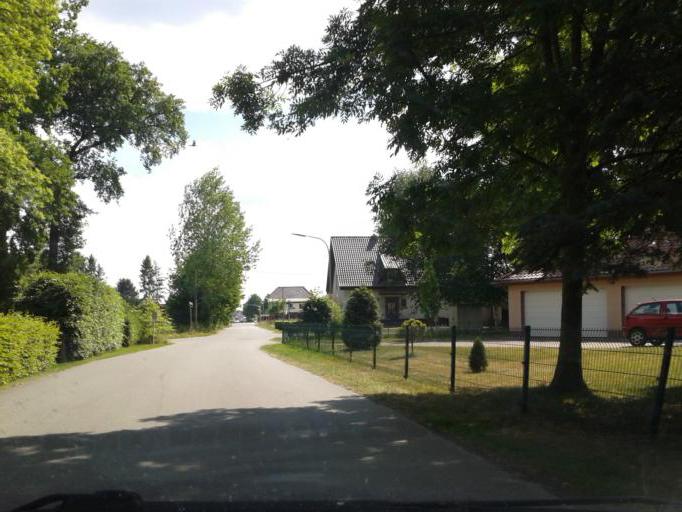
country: DE
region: North Rhine-Westphalia
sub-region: Regierungsbezirk Detmold
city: Paderborn
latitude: 51.7511
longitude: 8.6878
